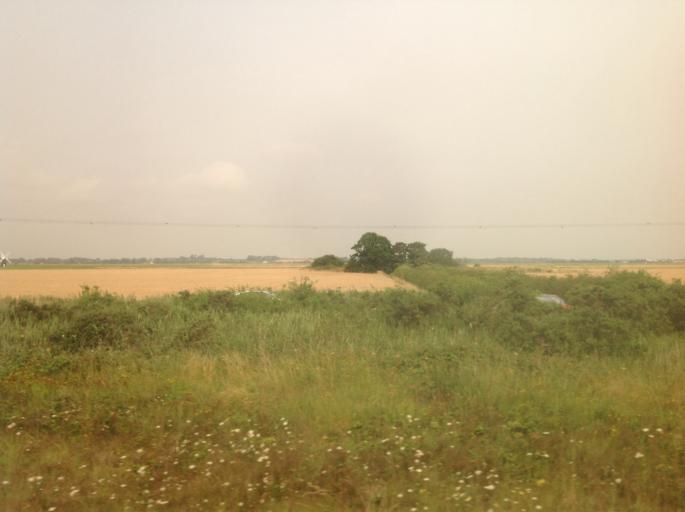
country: GB
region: England
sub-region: Norfolk
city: Great Yarmouth
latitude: 52.6198
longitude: 1.7068
